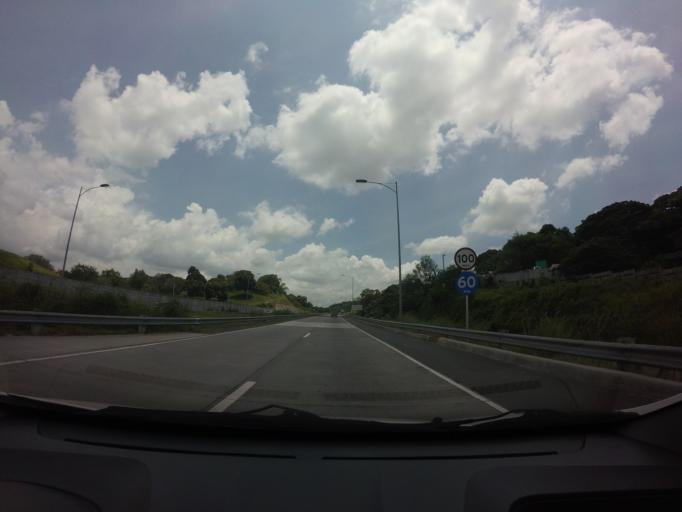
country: PH
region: Calabarzon
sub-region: Province of Laguna
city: San Pedro
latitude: 14.3834
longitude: 121.0375
